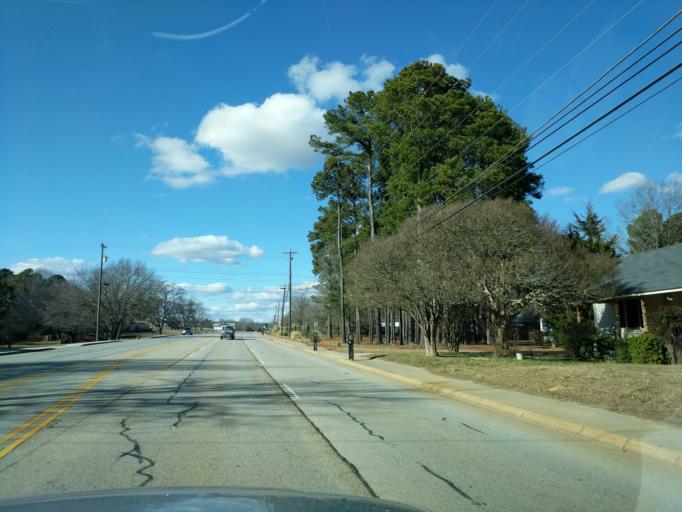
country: US
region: South Carolina
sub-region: Greenwood County
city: Greenwood
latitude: 34.1263
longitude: -82.1215
